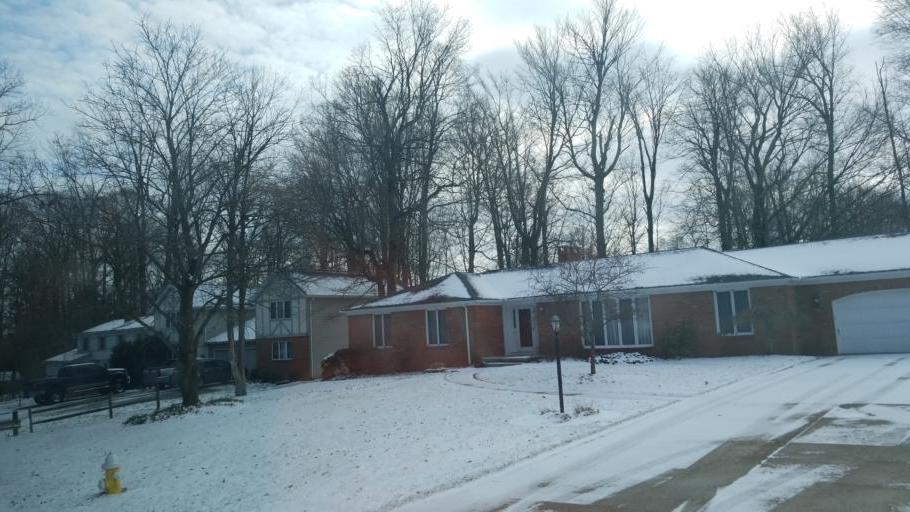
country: US
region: Ohio
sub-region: Richland County
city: Mansfield
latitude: 40.7185
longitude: -82.5412
